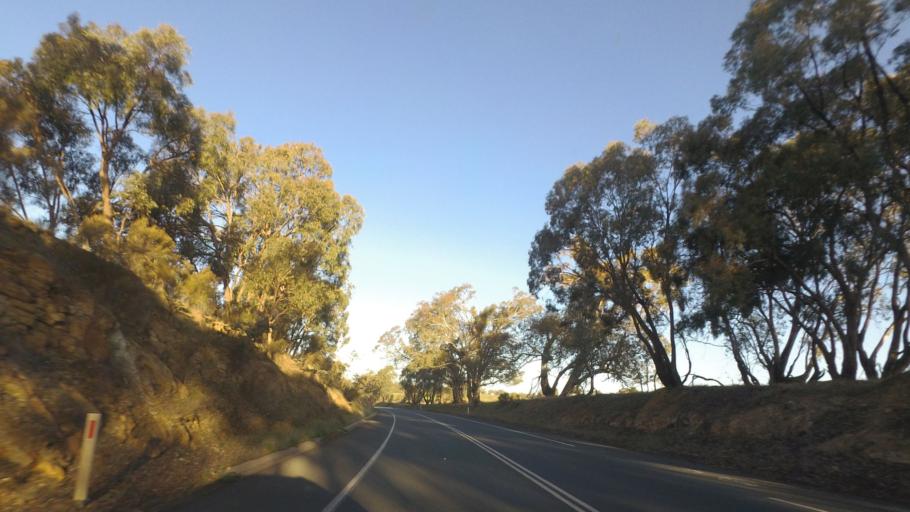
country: AU
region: Victoria
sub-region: Mount Alexander
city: Castlemaine
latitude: -37.0916
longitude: 144.5060
